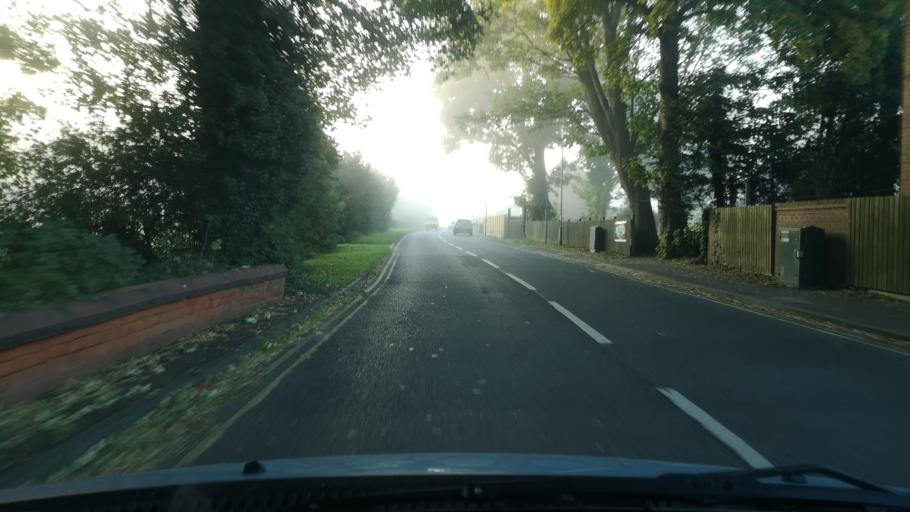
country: GB
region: England
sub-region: East Riding of Yorkshire
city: Skelton
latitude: 53.6905
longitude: -0.8322
